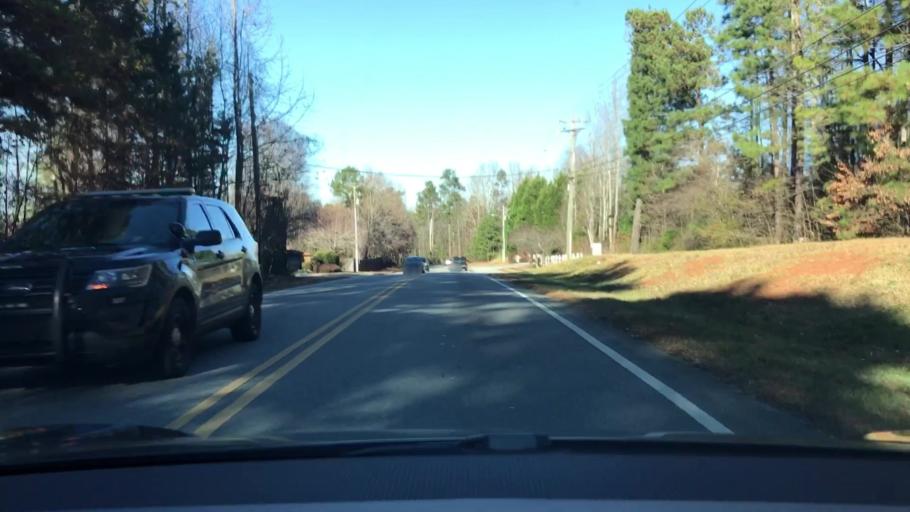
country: US
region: Georgia
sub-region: Barrow County
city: Auburn
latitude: 34.0945
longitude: -83.8673
